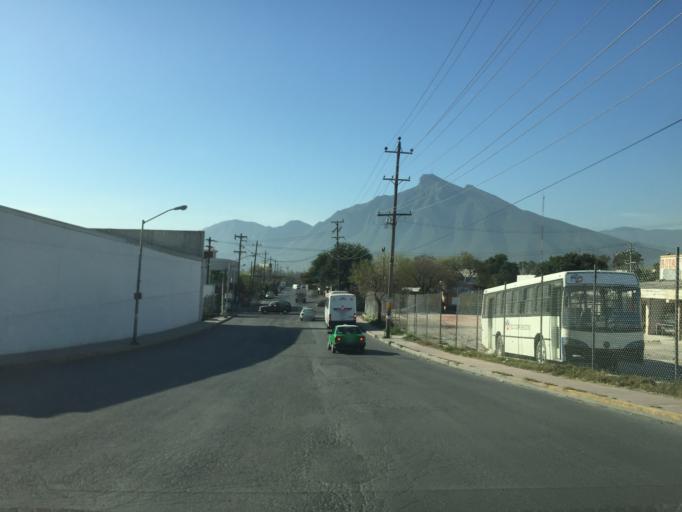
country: MX
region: Nuevo Leon
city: Guadalupe
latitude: 25.6959
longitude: -100.2172
